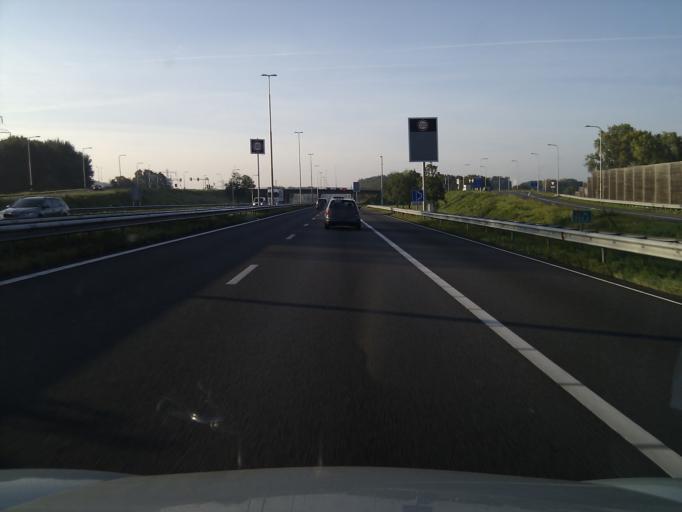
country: NL
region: Limburg
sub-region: Gemeente Sittard-Geleen
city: Born
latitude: 51.0427
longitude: 5.8257
